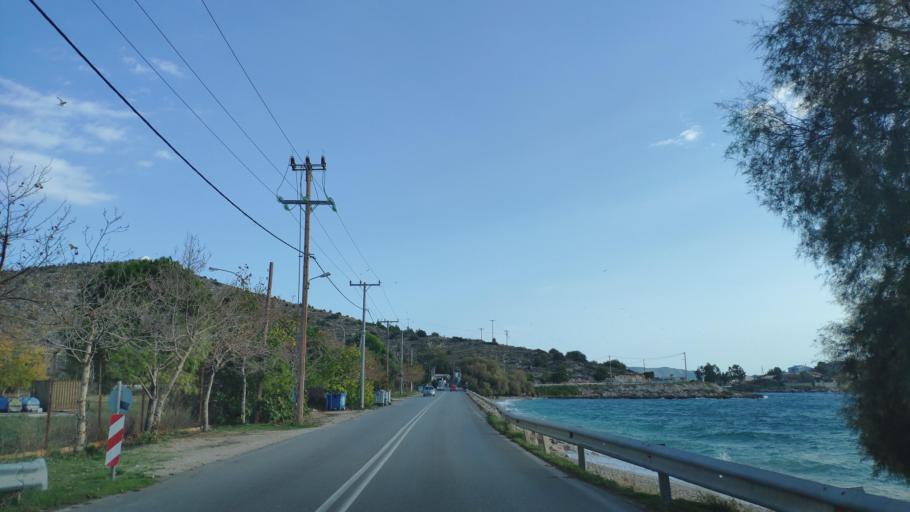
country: GR
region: Attica
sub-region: Nomarchia Dytikis Attikis
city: Megara
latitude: 37.9776
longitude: 23.3581
